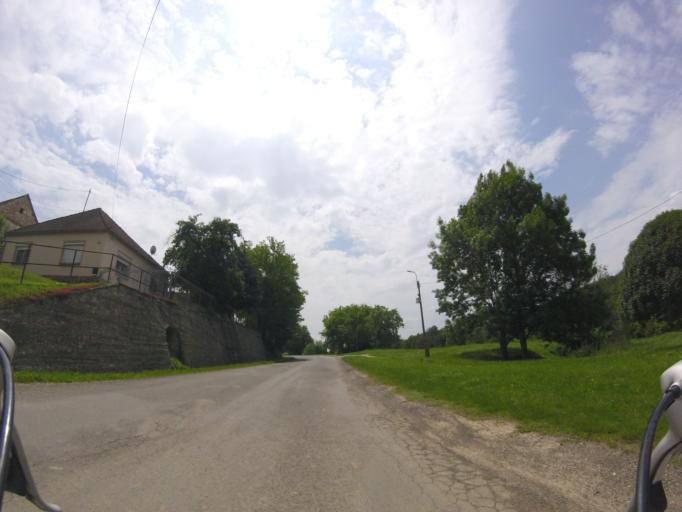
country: HU
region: Baranya
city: Kozarmisleny
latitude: 46.0183
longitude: 18.4085
